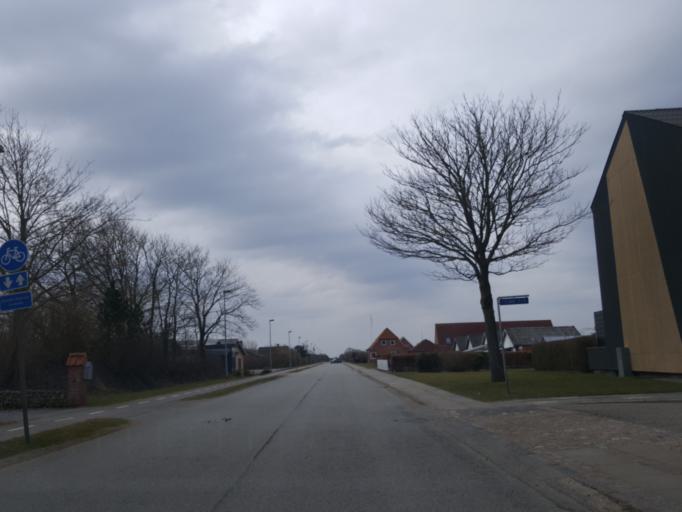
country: DK
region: Central Jutland
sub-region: Holstebro Kommune
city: Ulfborg
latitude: 56.3428
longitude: 8.3384
